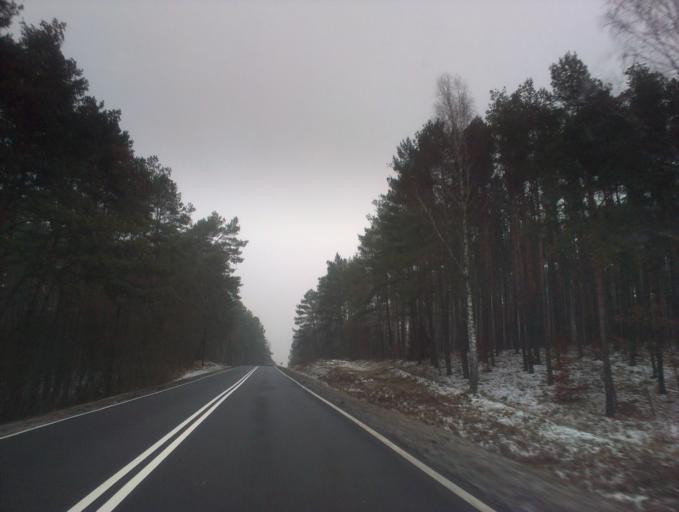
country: PL
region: Greater Poland Voivodeship
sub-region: Powiat zlotowski
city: Tarnowka
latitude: 53.2711
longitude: 16.7810
